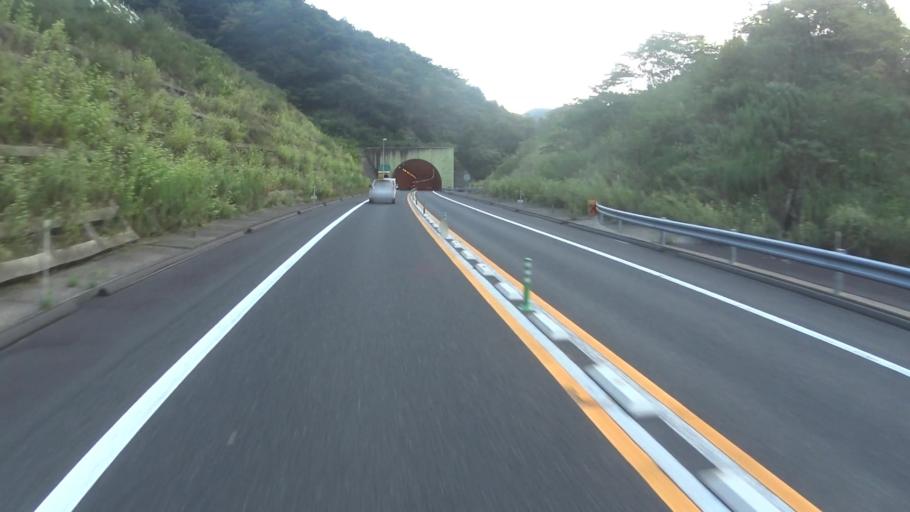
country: JP
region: Kyoto
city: Miyazu
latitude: 35.4706
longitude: 135.1755
